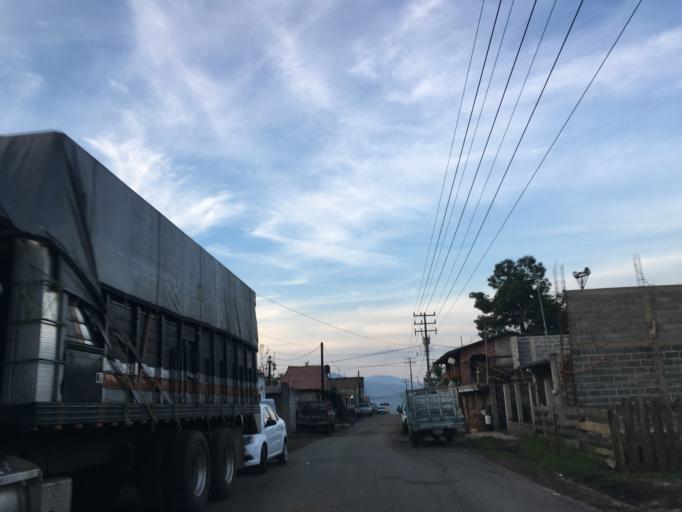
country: MX
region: Michoacan
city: Charapan
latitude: 19.6050
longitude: -102.2337
